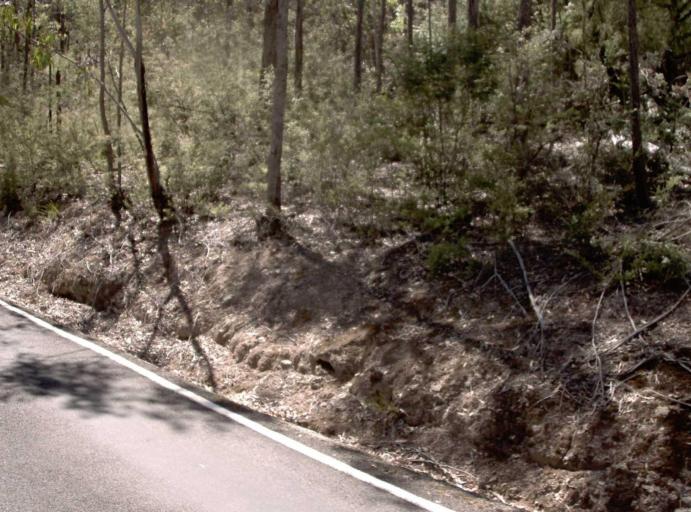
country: AU
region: Victoria
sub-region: East Gippsland
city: Lakes Entrance
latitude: -37.3857
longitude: 148.2183
